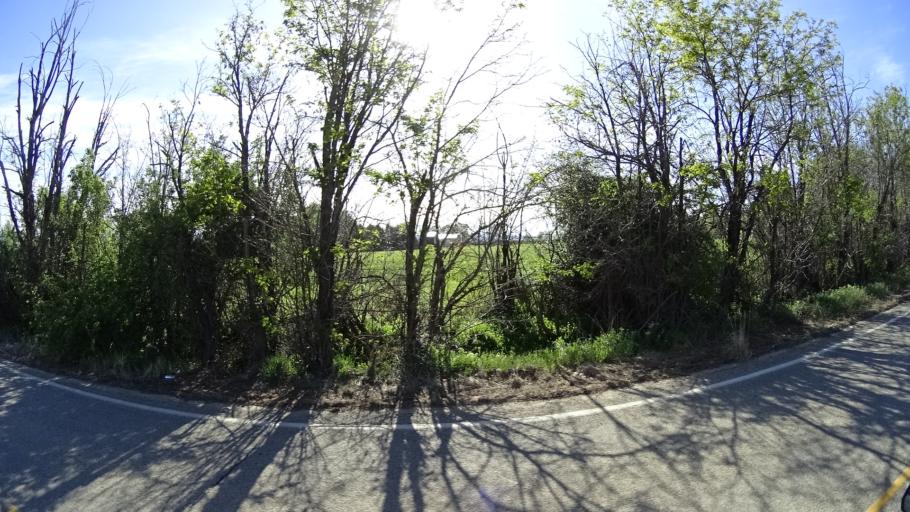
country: US
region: Idaho
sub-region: Ada County
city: Garden City
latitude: 43.5308
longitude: -116.2742
